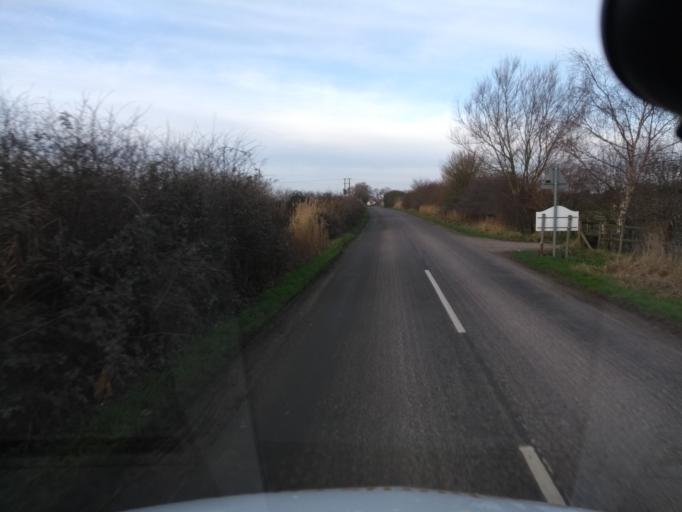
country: GB
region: England
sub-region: Somerset
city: Burnham-on-Sea
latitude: 51.2595
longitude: -2.9811
